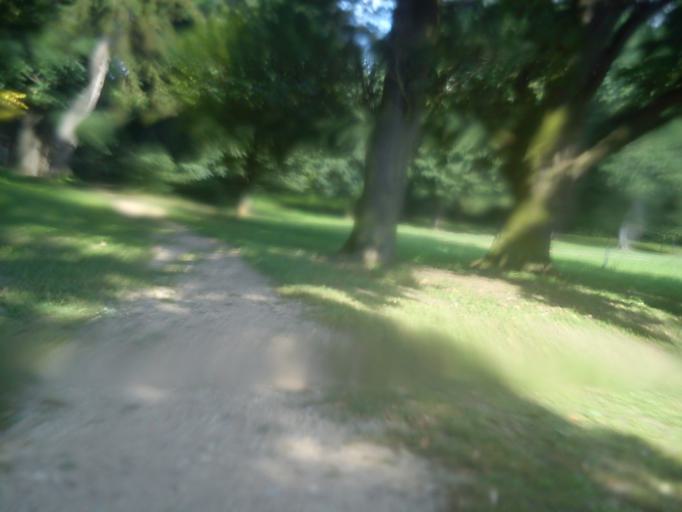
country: CZ
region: South Moravian
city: Sokolnice
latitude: 49.1202
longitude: 16.7263
